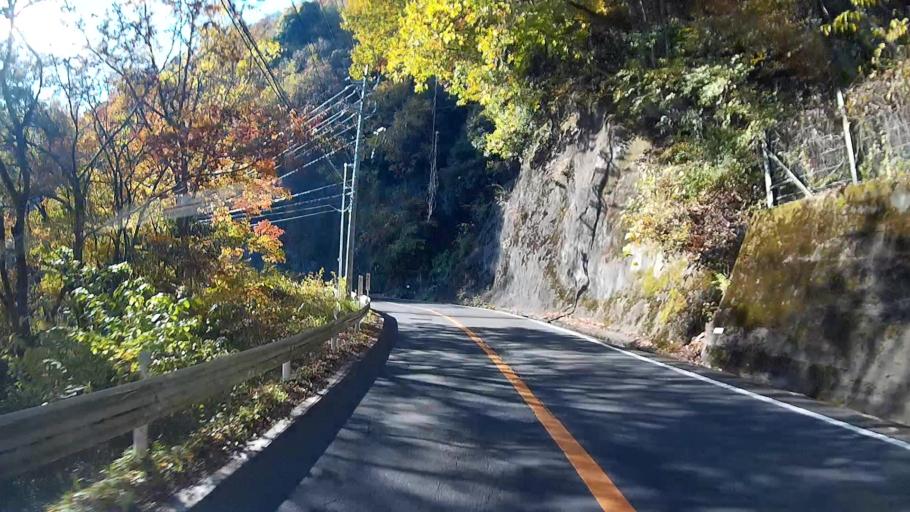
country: JP
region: Yamanashi
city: Uenohara
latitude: 35.6055
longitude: 139.1233
